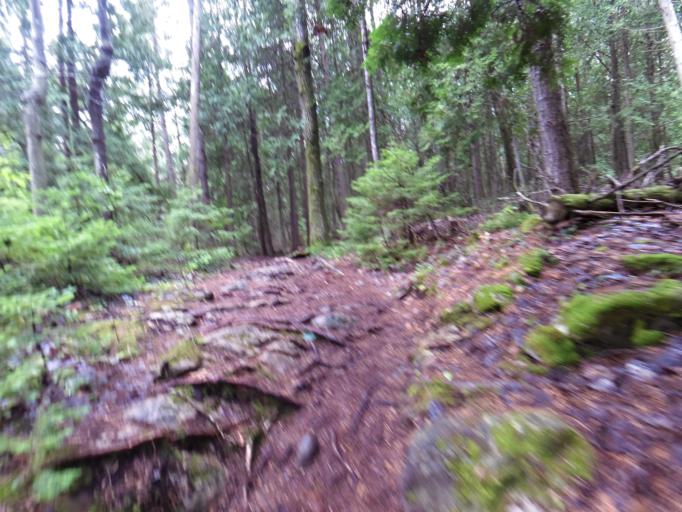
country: CA
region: Ontario
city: Tobermory
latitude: 45.2593
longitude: -81.6479
